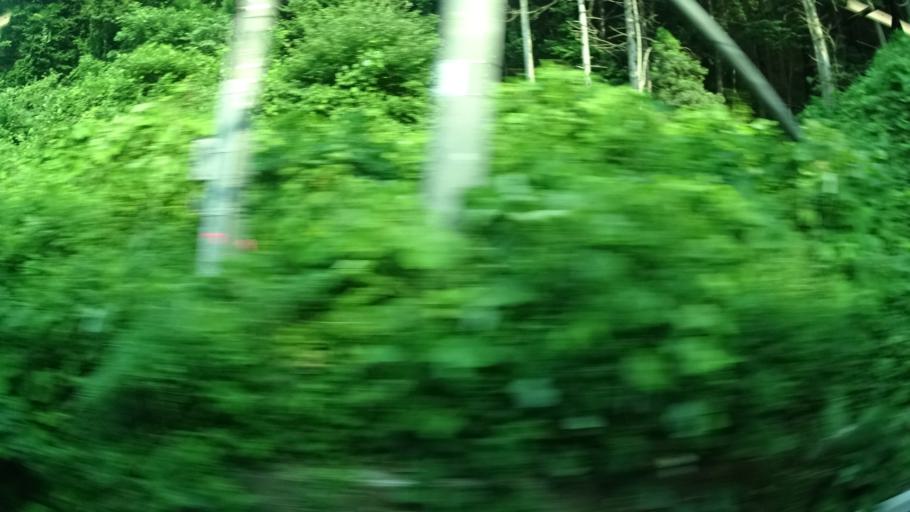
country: JP
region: Ibaraki
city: Kitaibaraki
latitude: 36.8629
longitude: 140.7861
